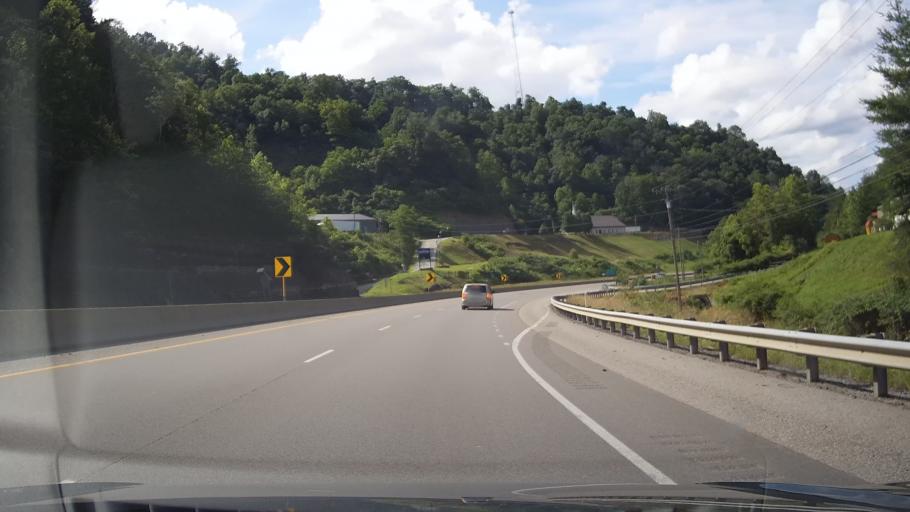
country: US
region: Kentucky
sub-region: Floyd County
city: Prestonsburg
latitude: 37.6500
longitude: -82.7845
